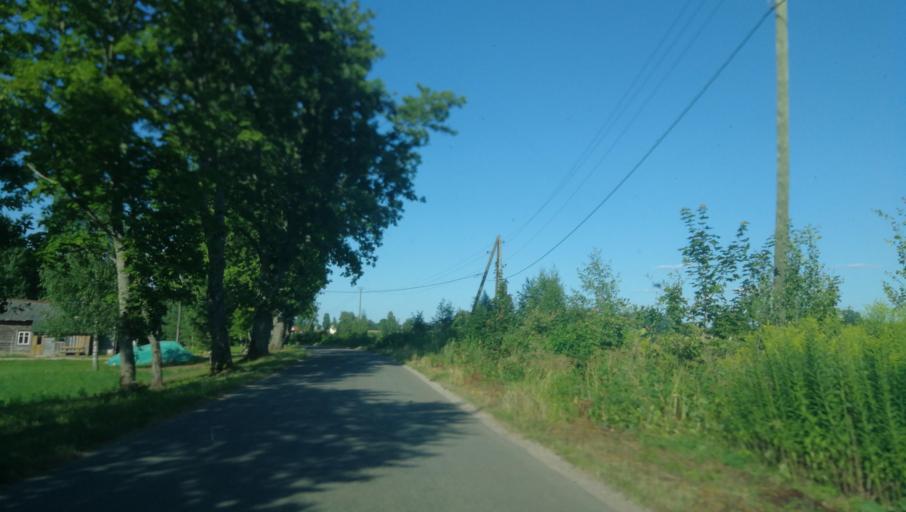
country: LV
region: Cesu Rajons
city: Cesis
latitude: 57.2886
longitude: 25.2287
